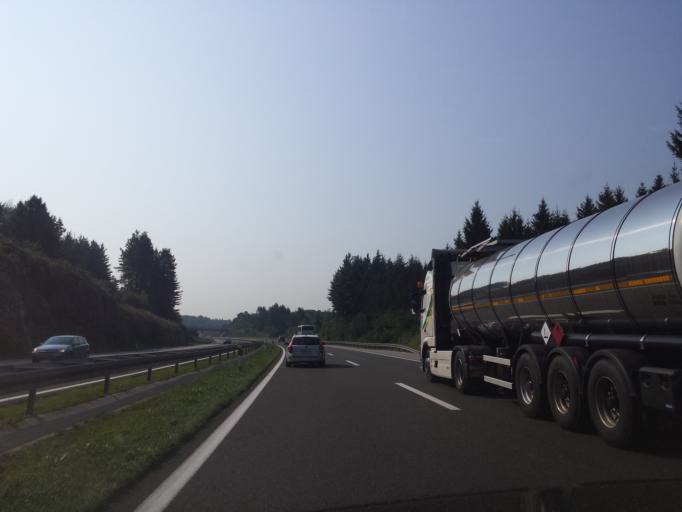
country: HR
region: Karlovacka
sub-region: Grad Ogulin
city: Ogulin
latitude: 45.3853
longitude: 15.2606
